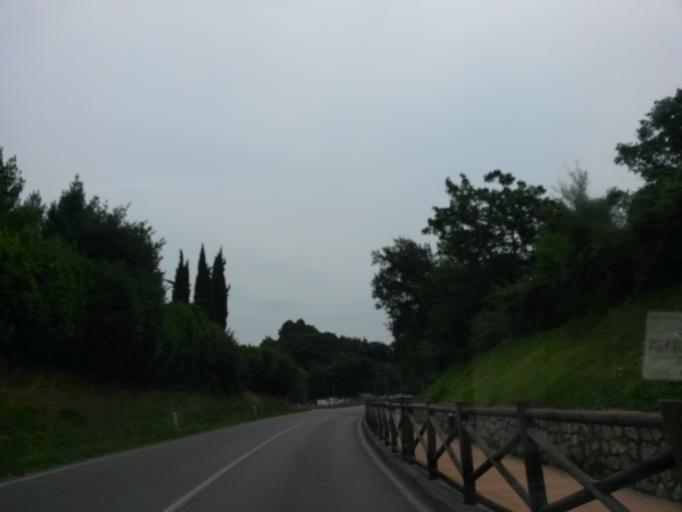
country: IT
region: Lombardy
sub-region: Provincia di Brescia
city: Cunettone-Villa
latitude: 45.5928
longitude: 10.5201
